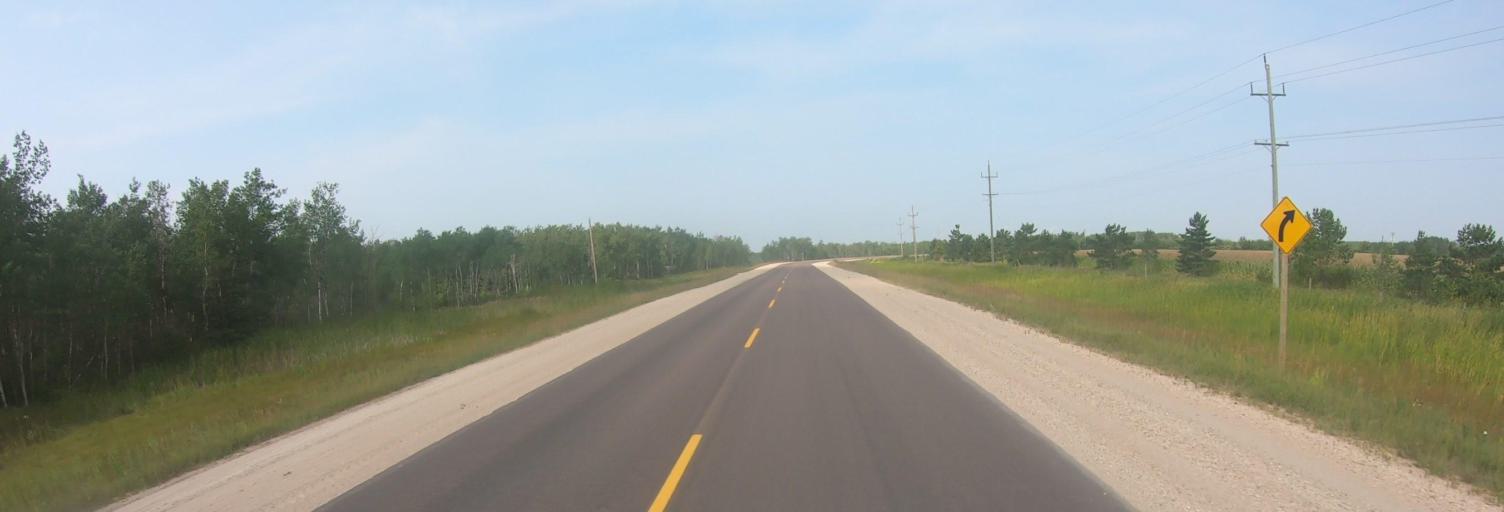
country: CA
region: Manitoba
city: La Broquerie
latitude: 49.2669
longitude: -96.4700
